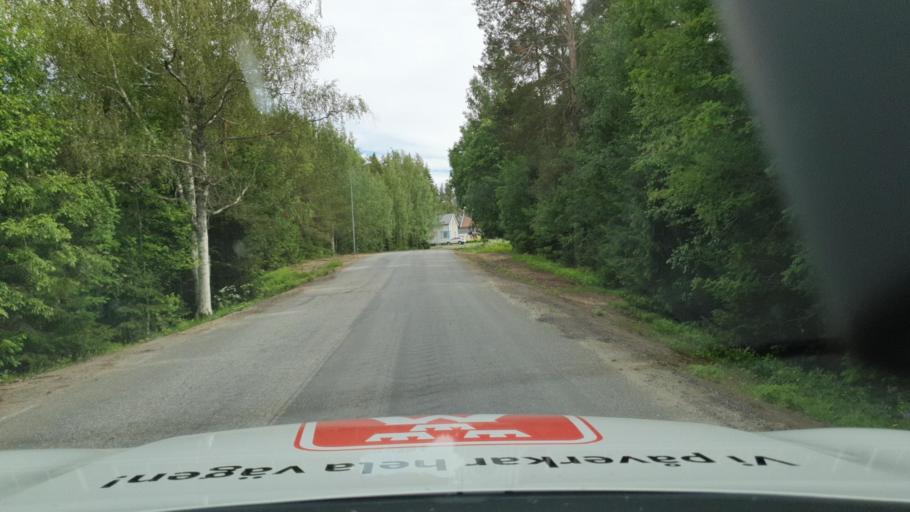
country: SE
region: Vaesterbotten
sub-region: Robertsfors Kommun
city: Robertsfors
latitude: 64.4097
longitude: 21.0032
